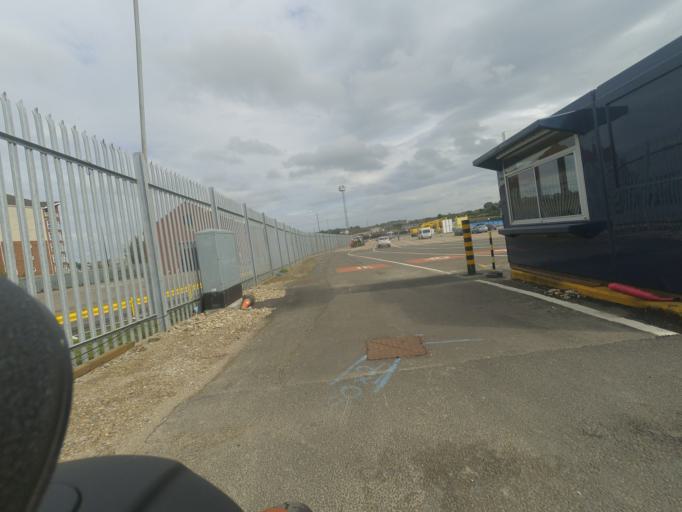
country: GB
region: England
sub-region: South Tyneside
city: South Shields
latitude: 54.9929
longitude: -1.4514
